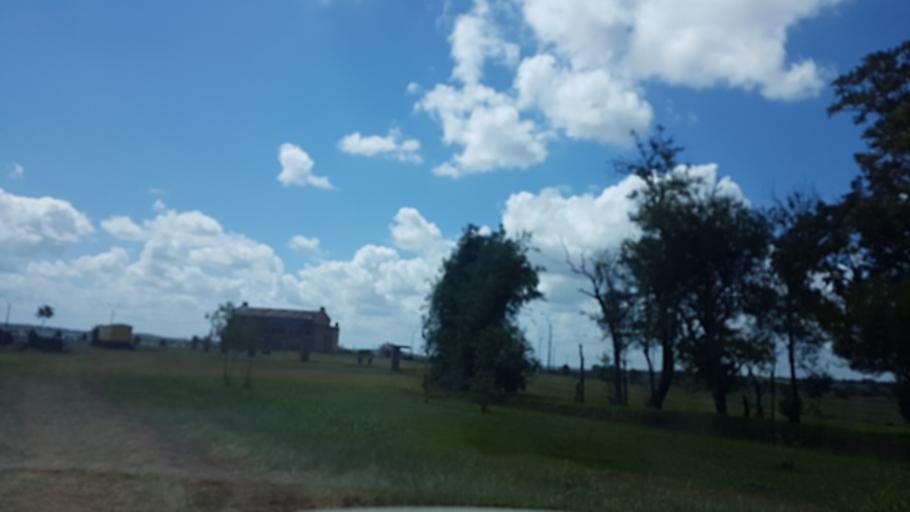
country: PY
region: Itapua
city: Carmen del Parana
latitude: -27.2185
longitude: -56.1507
